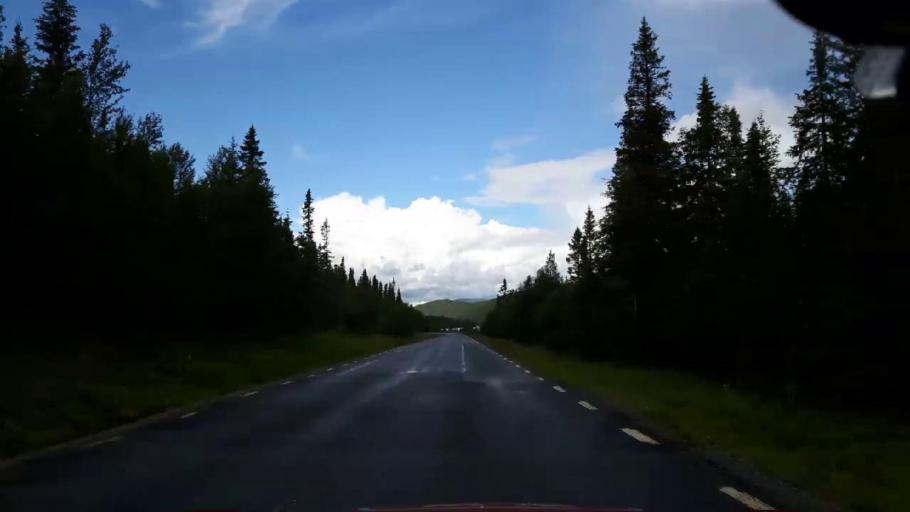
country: SE
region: Vaesterbotten
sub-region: Vilhelmina Kommun
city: Sjoberg
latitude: 65.0052
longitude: 15.1897
